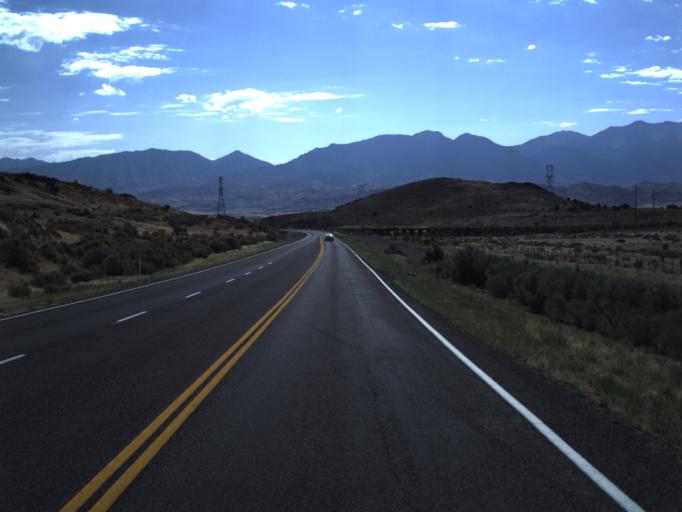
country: US
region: Utah
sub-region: Utah County
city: Genola
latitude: 39.9511
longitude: -112.0238
